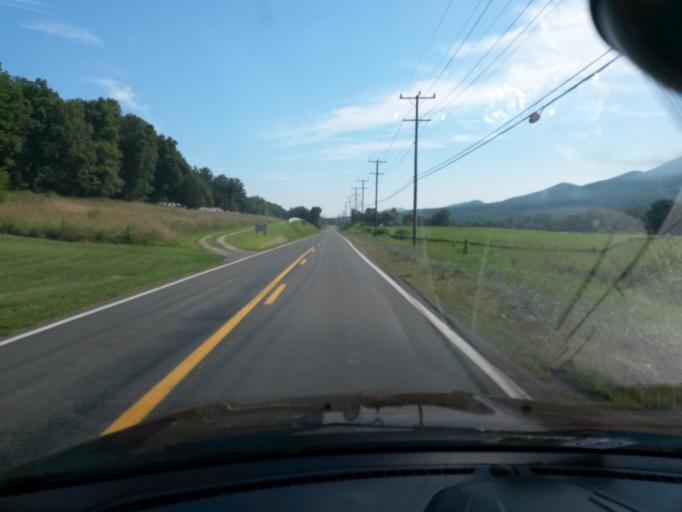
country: US
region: Virginia
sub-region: Shenandoah County
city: Basye
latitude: 38.8876
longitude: -78.8601
